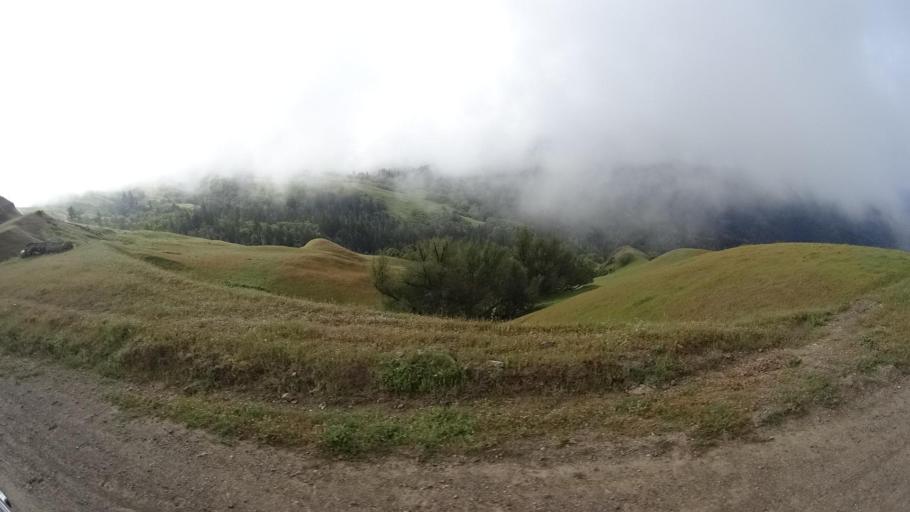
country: US
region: California
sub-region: Humboldt County
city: Redway
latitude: 40.2048
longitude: -123.7241
